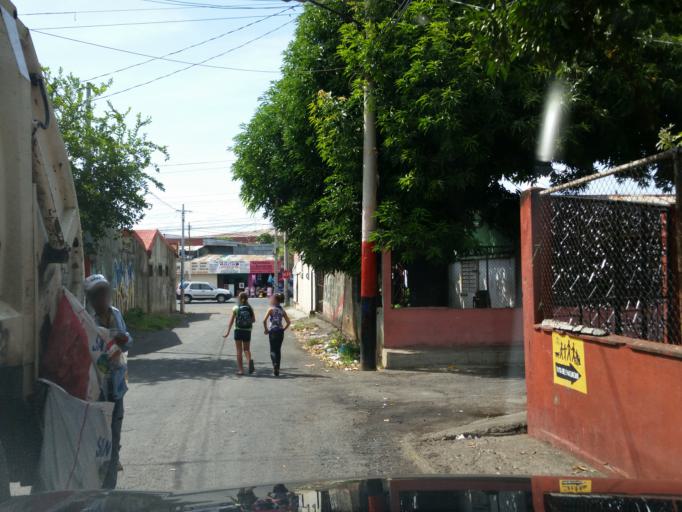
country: NI
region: Managua
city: Managua
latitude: 12.1451
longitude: -86.2494
